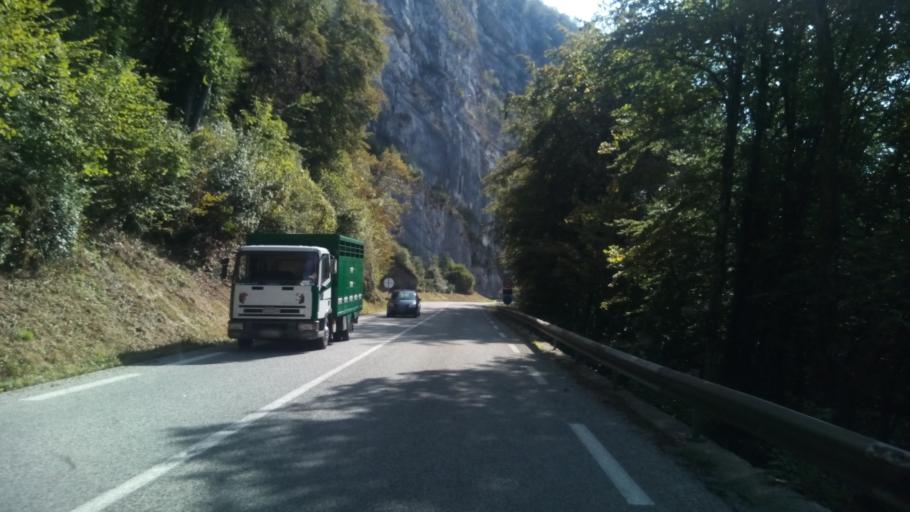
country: FR
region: Rhone-Alpes
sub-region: Departement de la Savoie
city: Les Echelles
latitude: 45.4556
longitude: 5.7874
